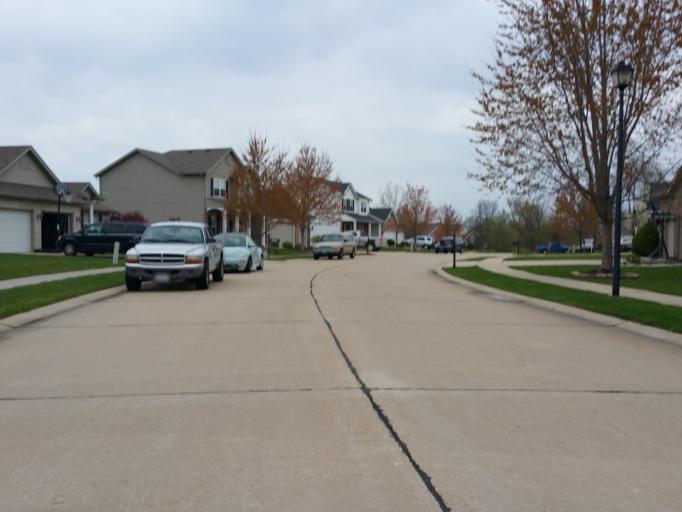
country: US
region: Illinois
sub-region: Madison County
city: Edwardsville
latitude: 38.7847
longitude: -89.9308
